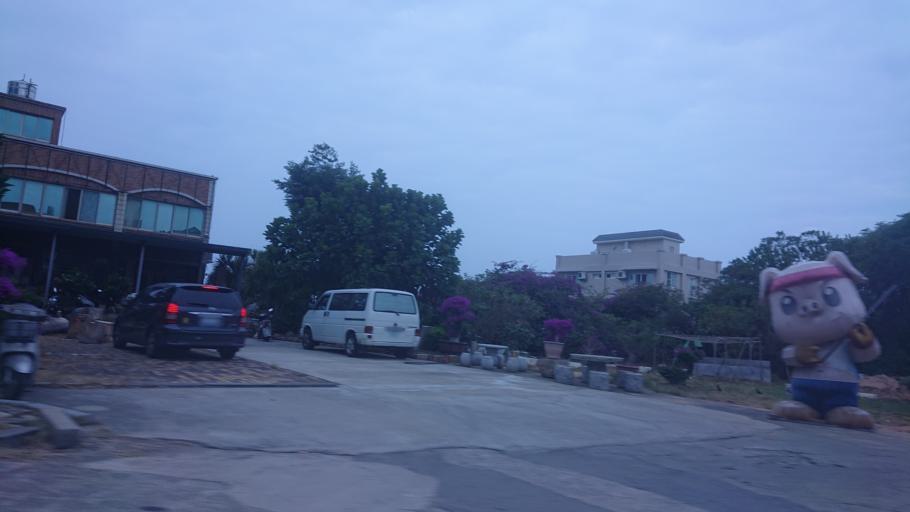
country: TW
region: Fukien
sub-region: Kinmen
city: Jincheng
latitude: 24.4424
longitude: 118.3118
